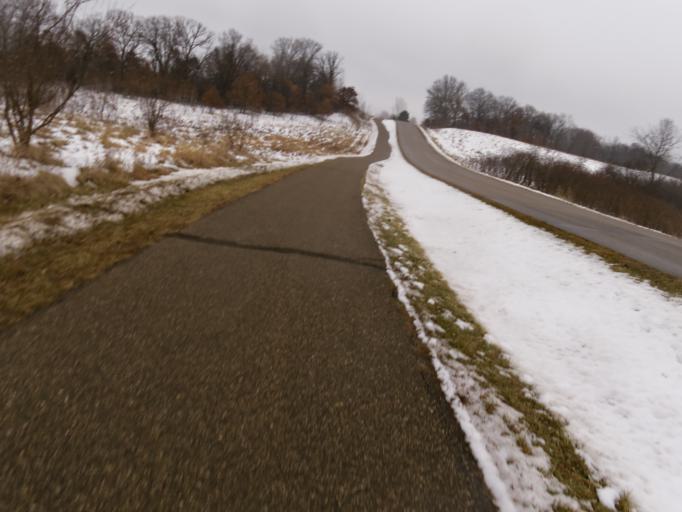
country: US
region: Minnesota
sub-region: Washington County
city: Lake Elmo
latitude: 44.9900
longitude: -92.8947
